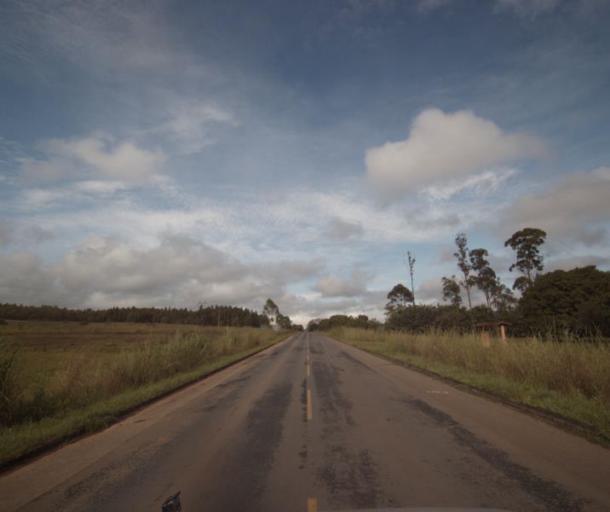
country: BR
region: Goias
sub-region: Pirenopolis
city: Pirenopolis
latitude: -15.7967
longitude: -48.7761
